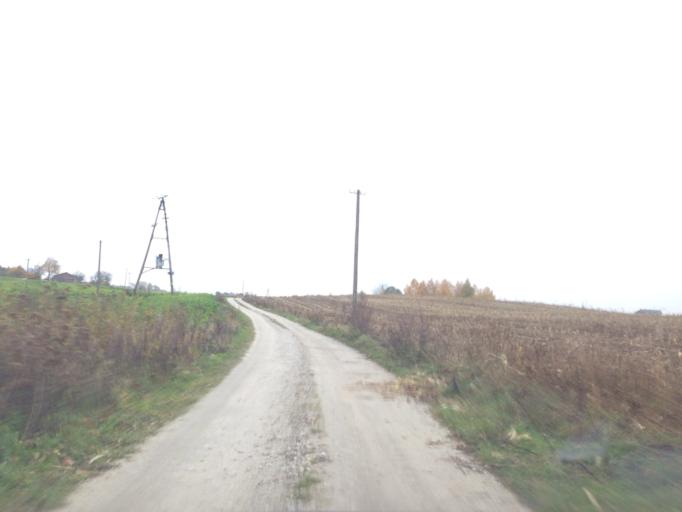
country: PL
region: Kujawsko-Pomorskie
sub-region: Powiat brodnicki
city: Bartniczka
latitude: 53.2145
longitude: 19.6048
